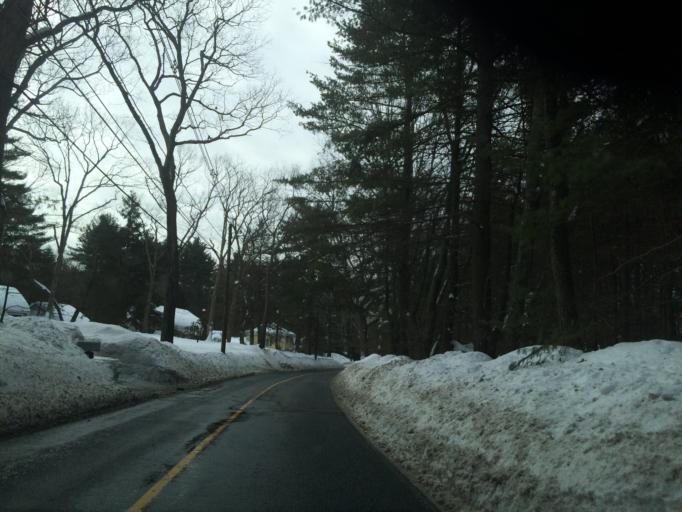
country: US
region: Massachusetts
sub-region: Middlesex County
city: Weston
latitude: 42.3848
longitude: -71.3084
